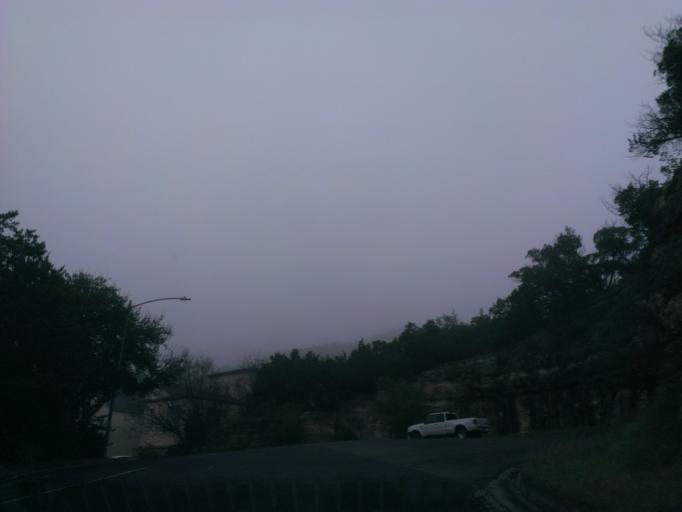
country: US
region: Texas
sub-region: Williamson County
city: Jollyville
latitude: 30.3734
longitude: -97.7911
